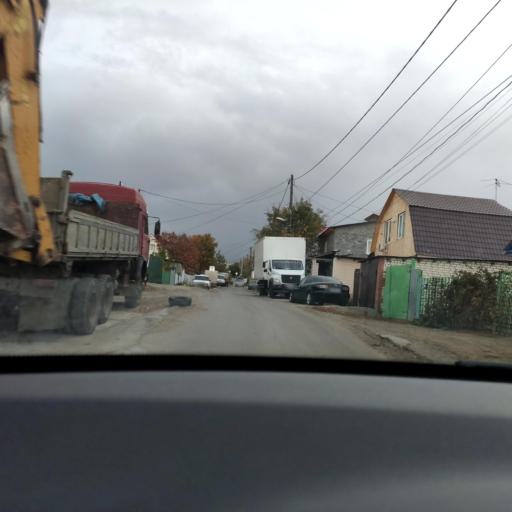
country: RU
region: Samara
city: Samara
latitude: 53.1839
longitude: 50.1862
